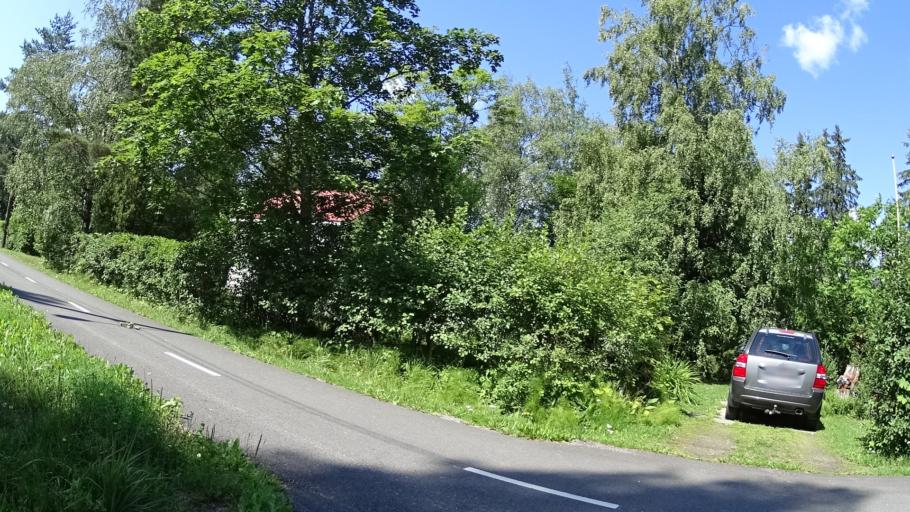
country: FI
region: Uusimaa
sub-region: Helsinki
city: Jaervenpaeae
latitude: 60.4682
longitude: 25.0696
